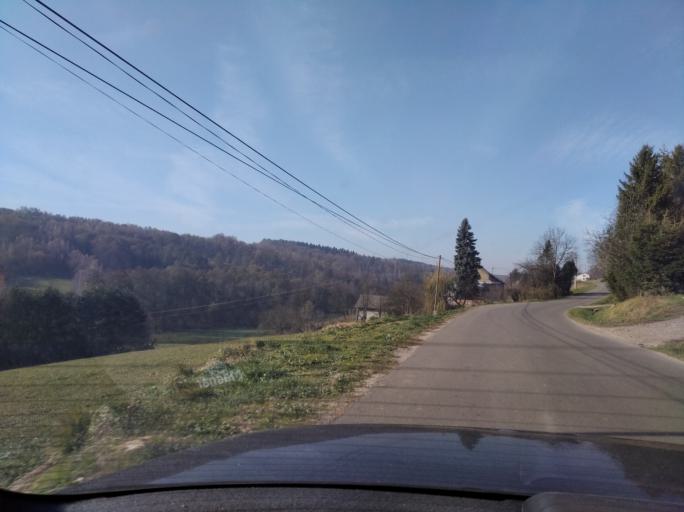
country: PL
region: Subcarpathian Voivodeship
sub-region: Powiat strzyzowski
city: Wisniowa
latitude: 49.8726
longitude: 21.6277
